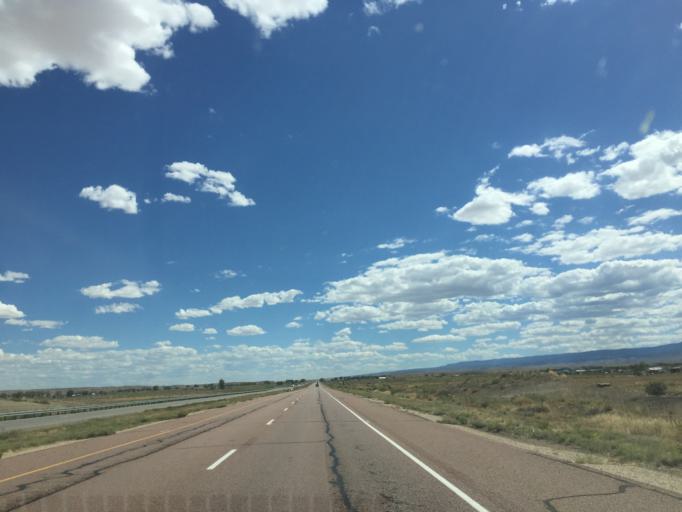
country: US
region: New Mexico
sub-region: San Juan County
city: Shiprock
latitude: 36.3139
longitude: -108.7084
